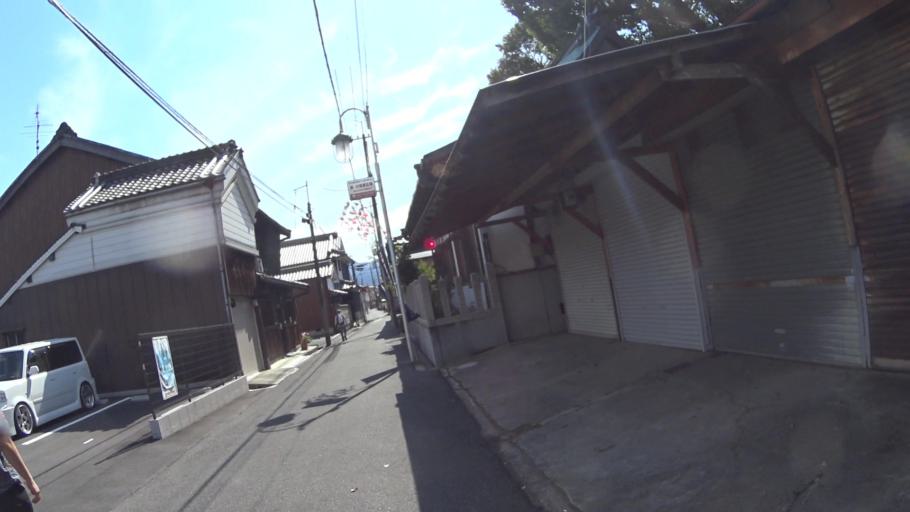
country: JP
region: Nara
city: Sakurai
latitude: 34.5267
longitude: 135.8476
